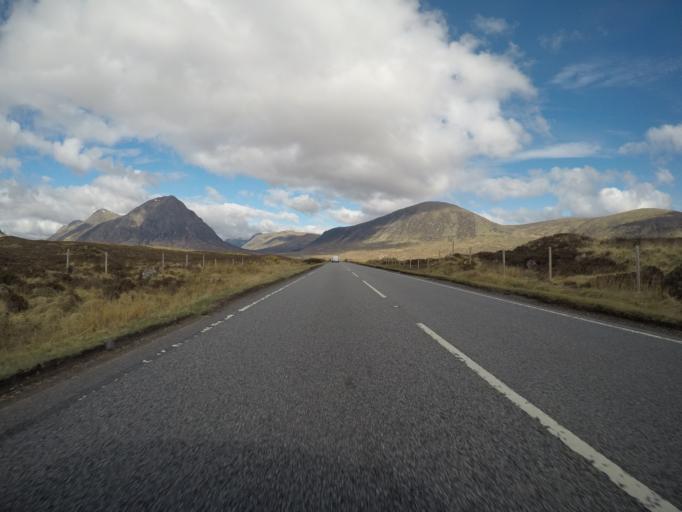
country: GB
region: Scotland
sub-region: Highland
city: Spean Bridge
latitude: 56.6444
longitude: -4.8304
